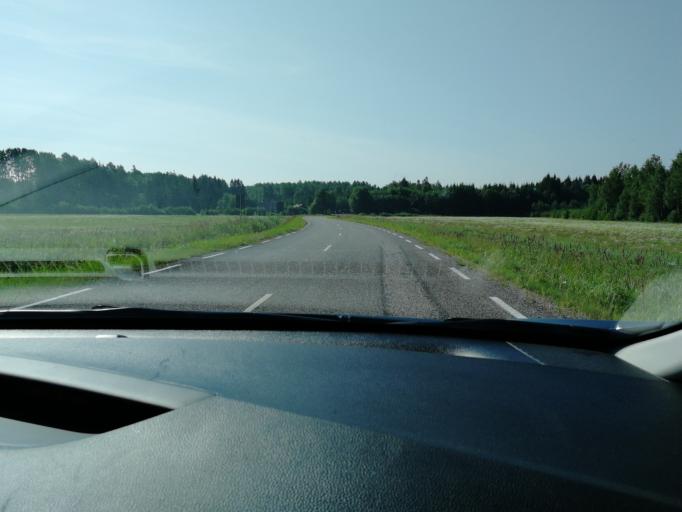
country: EE
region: Paernumaa
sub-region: Saarde vald
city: Kilingi-Nomme
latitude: 58.0172
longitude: 25.0077
